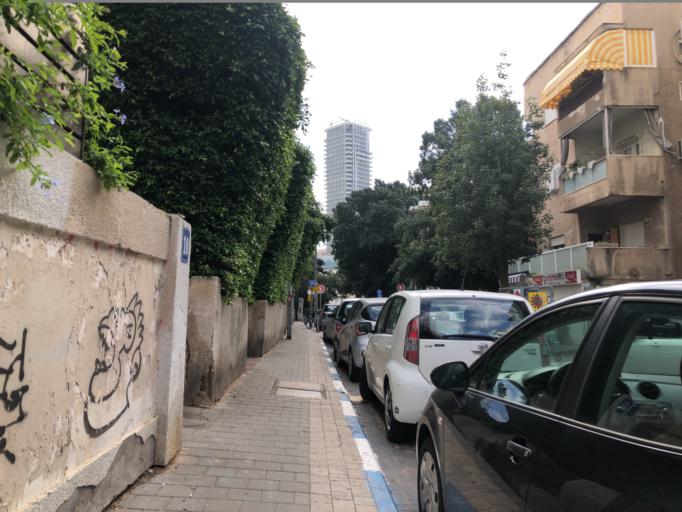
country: IL
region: Tel Aviv
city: Tel Aviv
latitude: 32.0671
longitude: 34.7752
